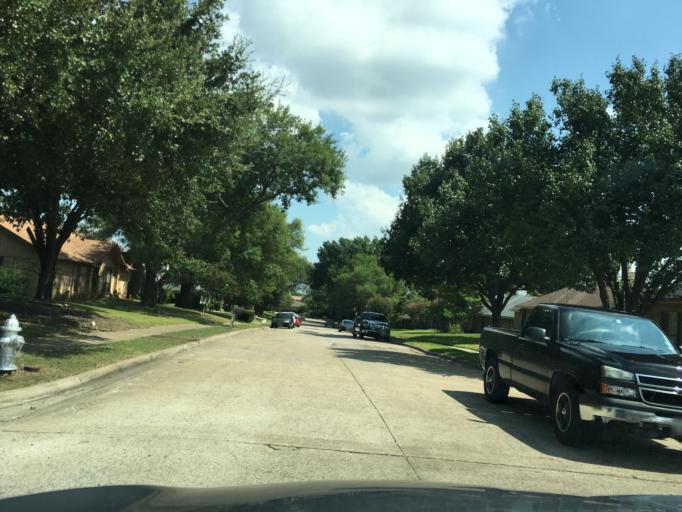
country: US
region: Texas
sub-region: Dallas County
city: Garland
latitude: 32.9491
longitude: -96.6379
